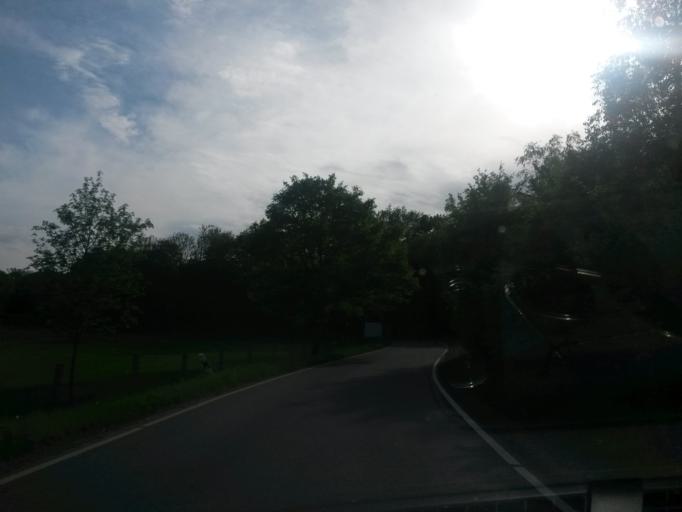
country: DE
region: North Rhine-Westphalia
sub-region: Regierungsbezirk Arnsberg
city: Hagen
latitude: 51.3478
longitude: 7.5289
